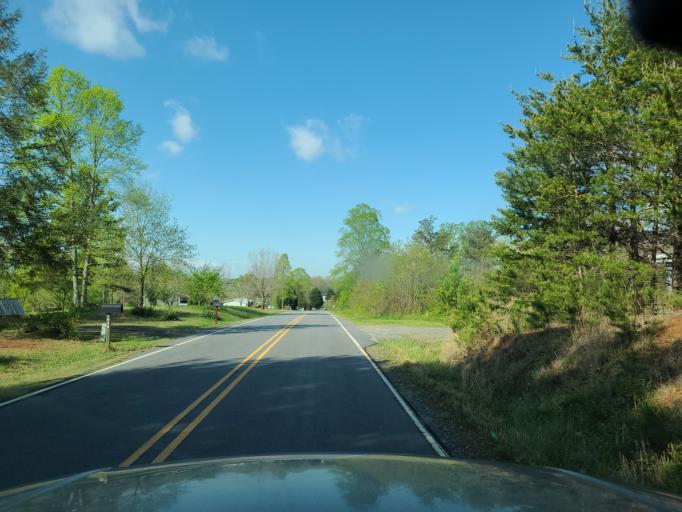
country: US
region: North Carolina
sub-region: Rutherford County
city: Spindale
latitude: 35.3963
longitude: -81.9068
